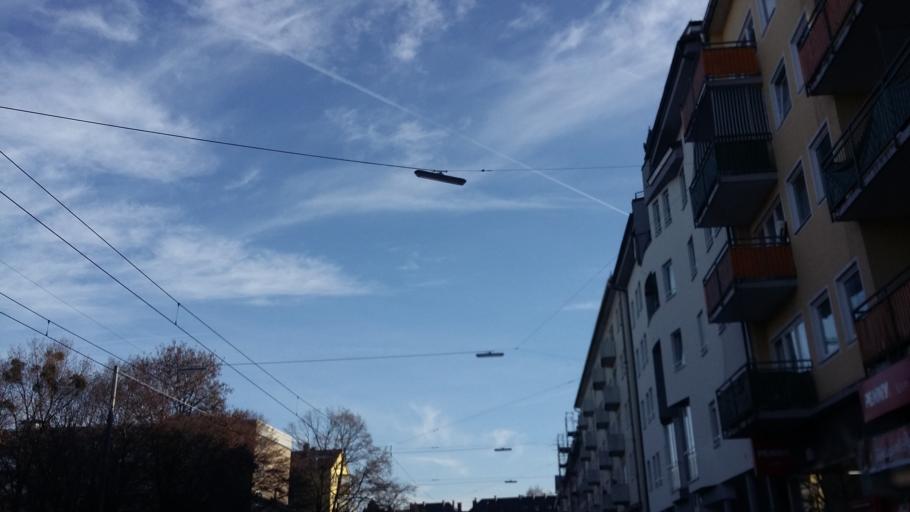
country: DE
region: Bavaria
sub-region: Upper Bavaria
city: Pasing
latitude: 48.1390
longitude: 11.5148
